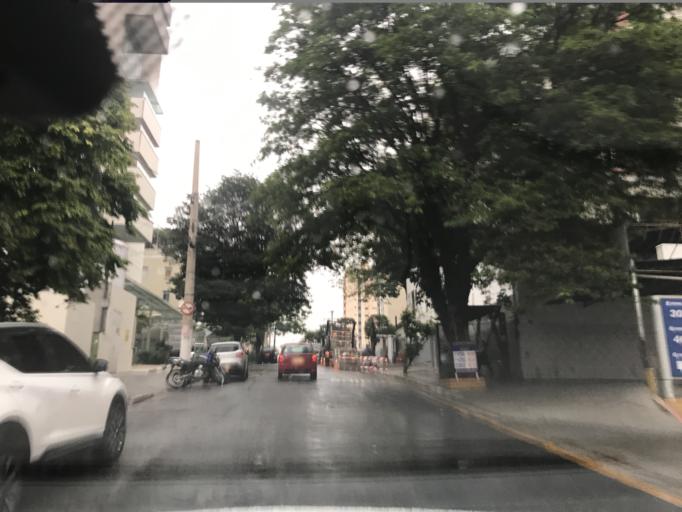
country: BR
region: Sao Paulo
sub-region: Sao Paulo
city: Sao Paulo
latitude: -23.5332
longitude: -46.6885
